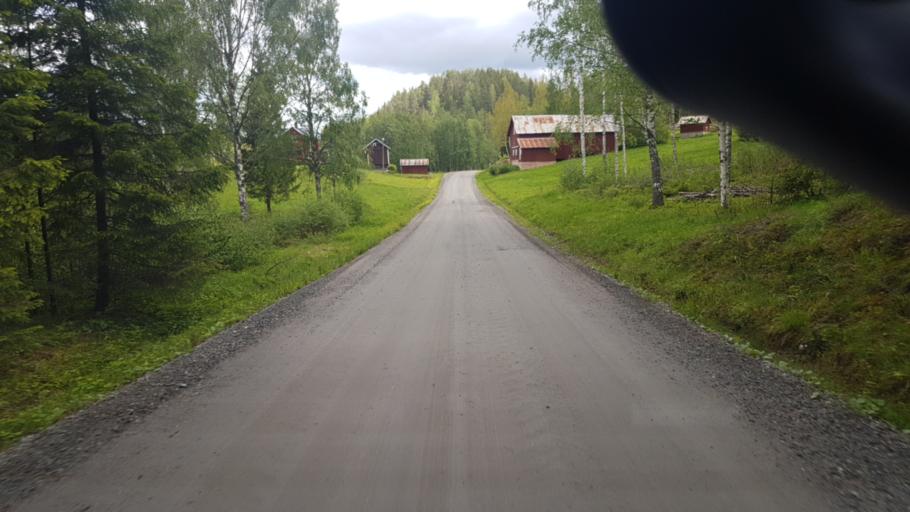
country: NO
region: Ostfold
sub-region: Romskog
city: Romskog
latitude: 59.6903
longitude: 11.9402
